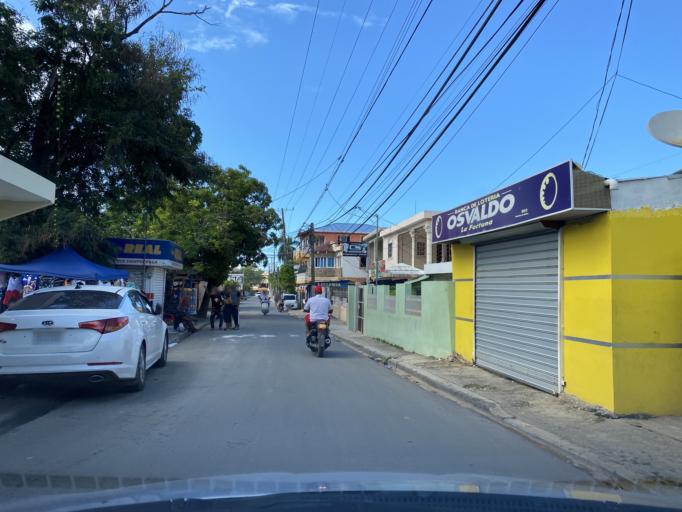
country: DO
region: Samana
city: Las Terrenas
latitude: 19.3111
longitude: -69.5445
